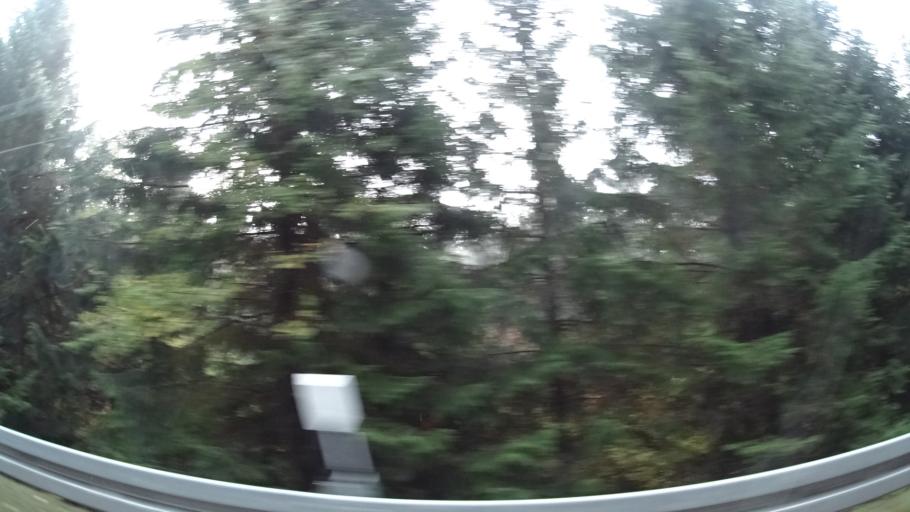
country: DE
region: Hesse
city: Gedern
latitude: 50.4624
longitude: 9.2606
